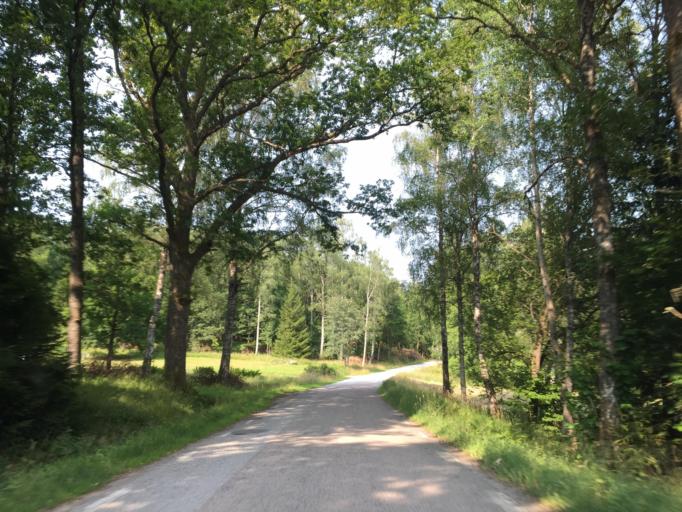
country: SE
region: Vaestra Goetaland
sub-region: Trollhattan
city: Sjuntorp
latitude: 58.2846
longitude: 12.1245
